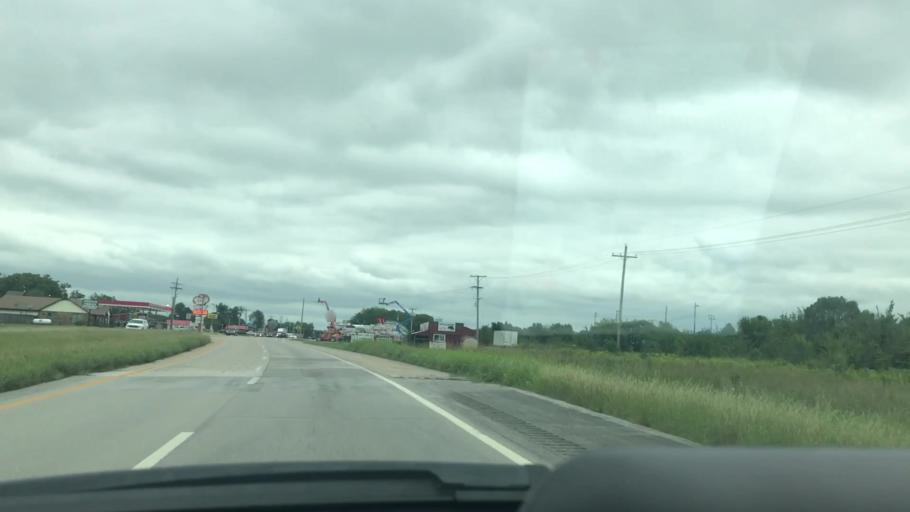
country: US
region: Oklahoma
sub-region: Mayes County
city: Pryor
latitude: 36.4319
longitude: -95.2736
